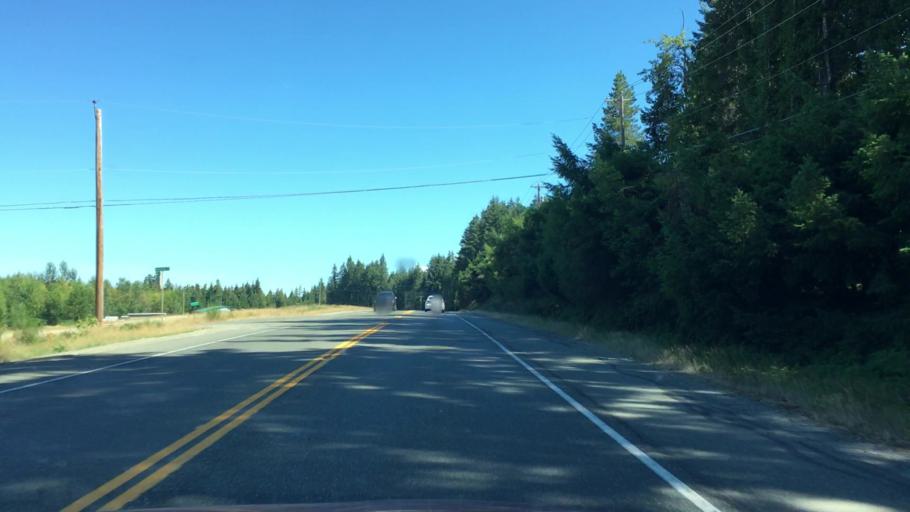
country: CA
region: British Columbia
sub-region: Regional District of Nanaimo
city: Parksville
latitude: 49.3087
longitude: -124.4934
